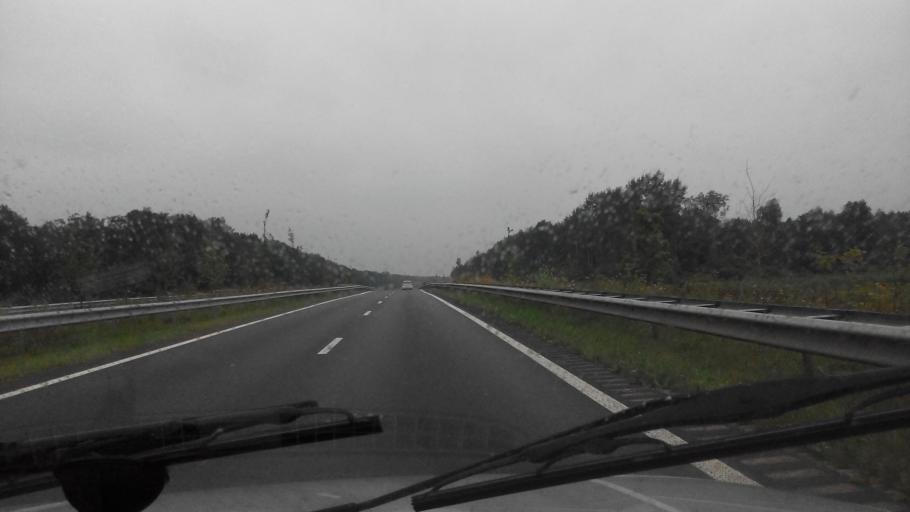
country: NL
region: Flevoland
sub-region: Gemeente Zeewolde
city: Zeewolde
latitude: 52.3409
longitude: 5.4898
